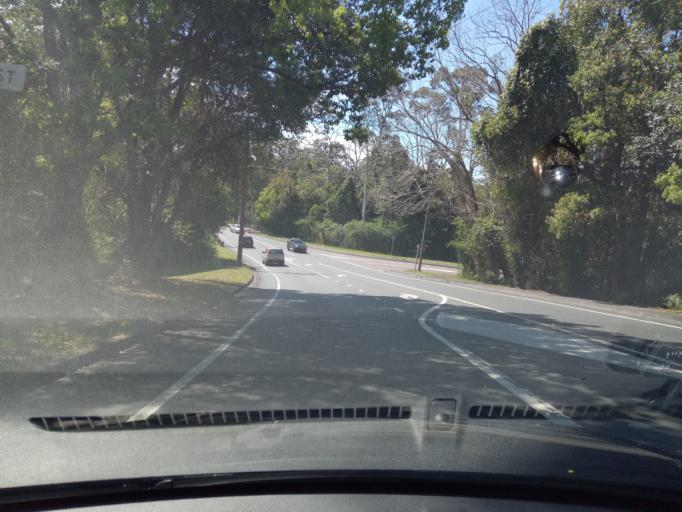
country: AU
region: New South Wales
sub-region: Gosford Shire
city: Narara
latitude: -33.4027
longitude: 151.3427
